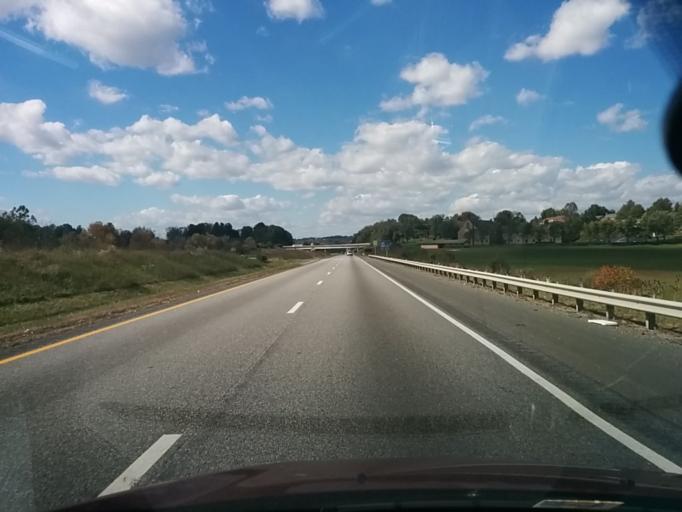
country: US
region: Virginia
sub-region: City of Waynesboro
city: Waynesboro
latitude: 38.0512
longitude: -78.9135
